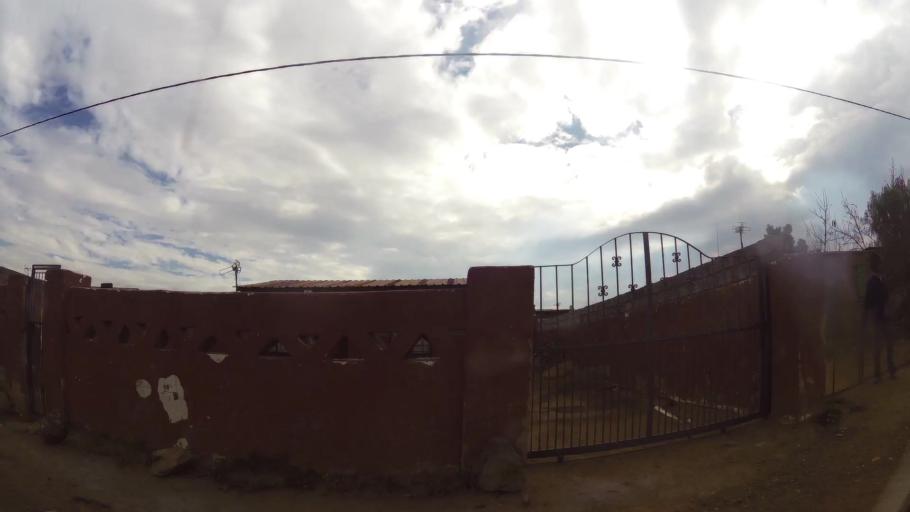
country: ZA
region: Gauteng
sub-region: Ekurhuleni Metropolitan Municipality
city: Germiston
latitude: -26.4026
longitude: 28.1474
